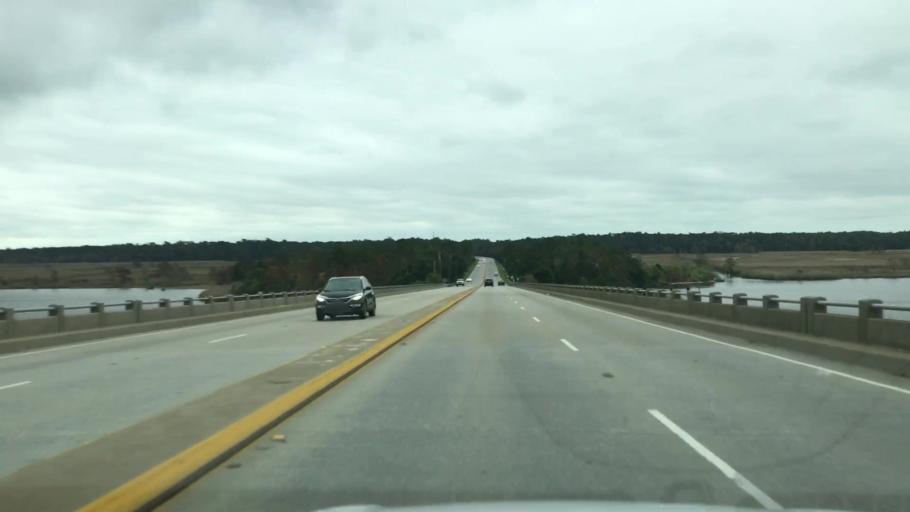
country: US
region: South Carolina
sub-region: Georgetown County
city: Georgetown
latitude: 33.3655
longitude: -79.2512
